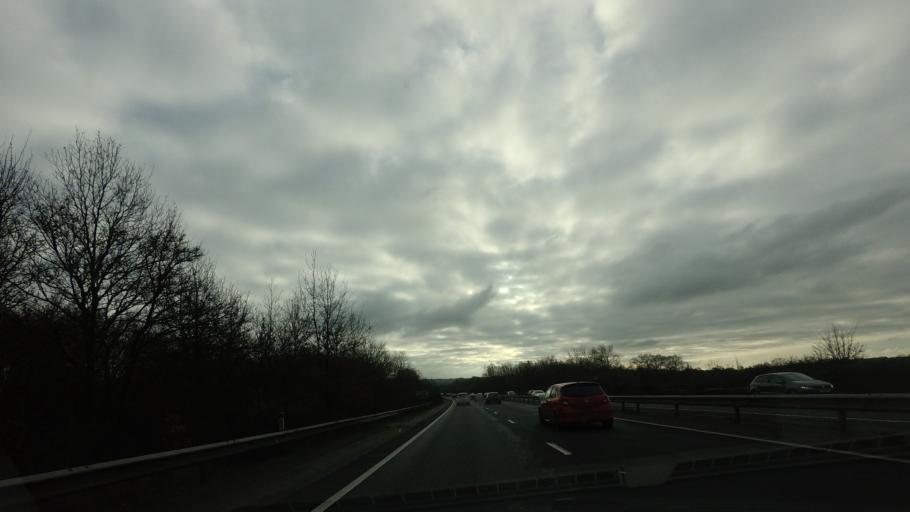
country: GB
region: England
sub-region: Kent
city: Tonbridge
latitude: 51.2103
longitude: 0.2255
